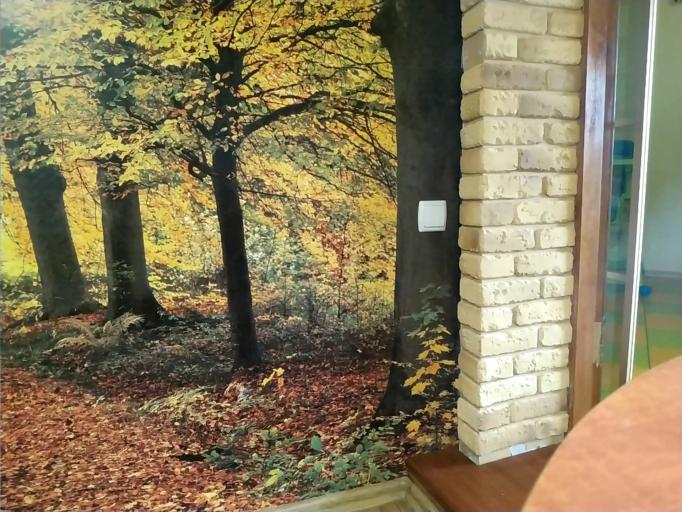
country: RU
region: Smolensk
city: Dorogobuzh
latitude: 54.8700
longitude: 33.3111
